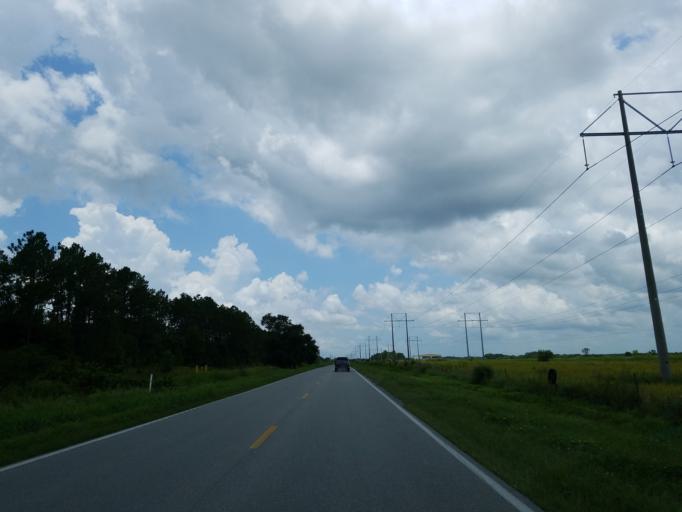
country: US
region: Florida
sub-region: Polk County
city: Willow Oak
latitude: 27.8507
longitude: -82.0423
